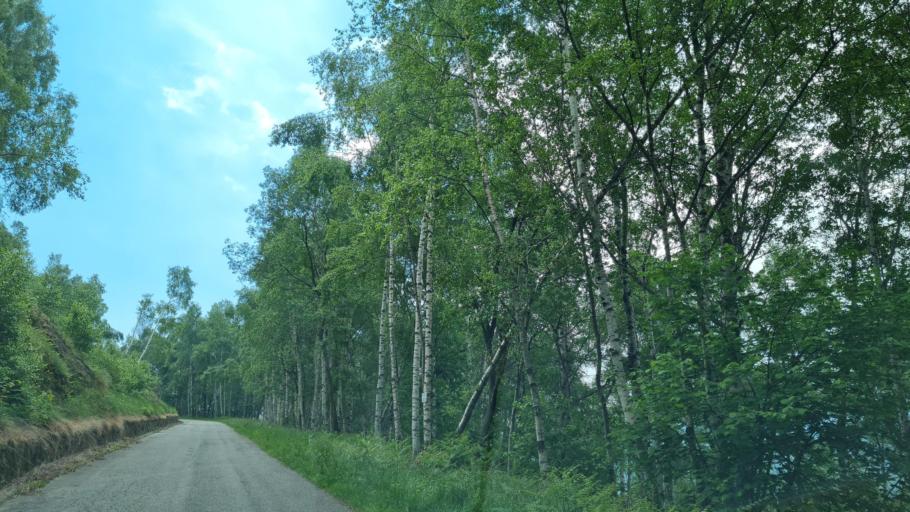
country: IT
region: Piedmont
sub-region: Provincia di Biella
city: Sordevolo
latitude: 45.5924
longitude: 7.9558
